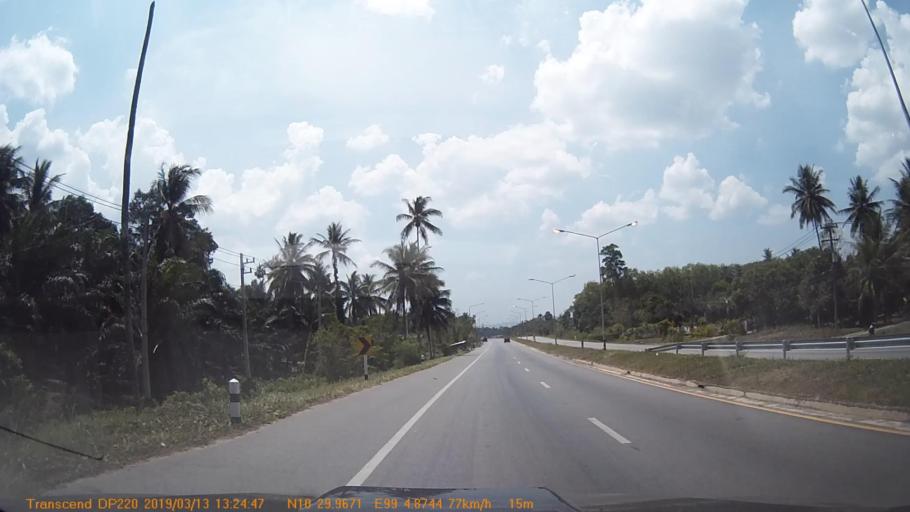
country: TH
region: Chumphon
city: Chumphon
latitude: 10.5012
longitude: 99.0852
